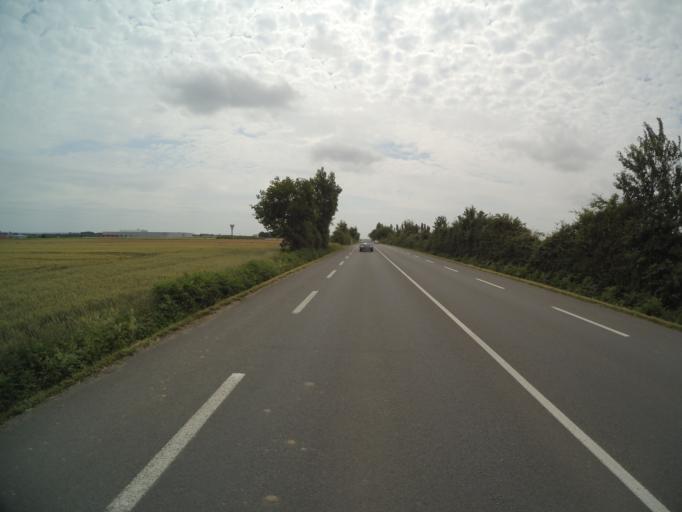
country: FR
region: Pays de la Loire
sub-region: Departement de la Vendee
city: Chavagnes-en-Paillers
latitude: 46.9188
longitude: -1.2456
